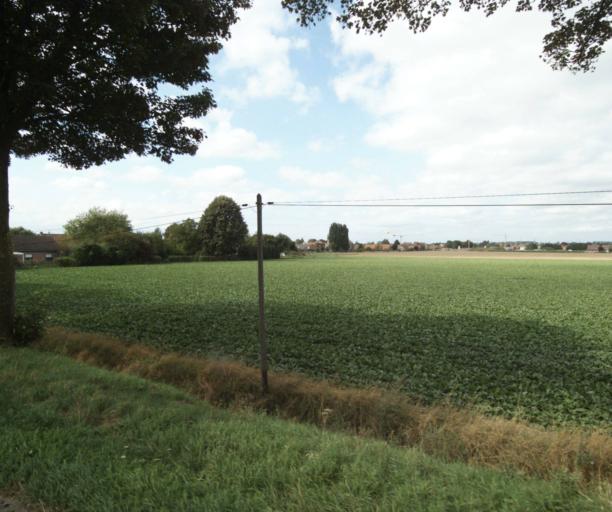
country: FR
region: Nord-Pas-de-Calais
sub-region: Departement du Nord
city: Baisieux
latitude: 50.6093
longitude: 3.2327
